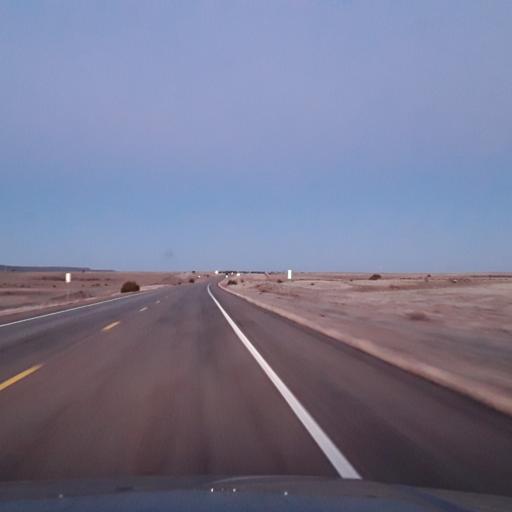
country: US
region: New Mexico
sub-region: Guadalupe County
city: Santa Rosa
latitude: 34.7415
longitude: -105.0231
